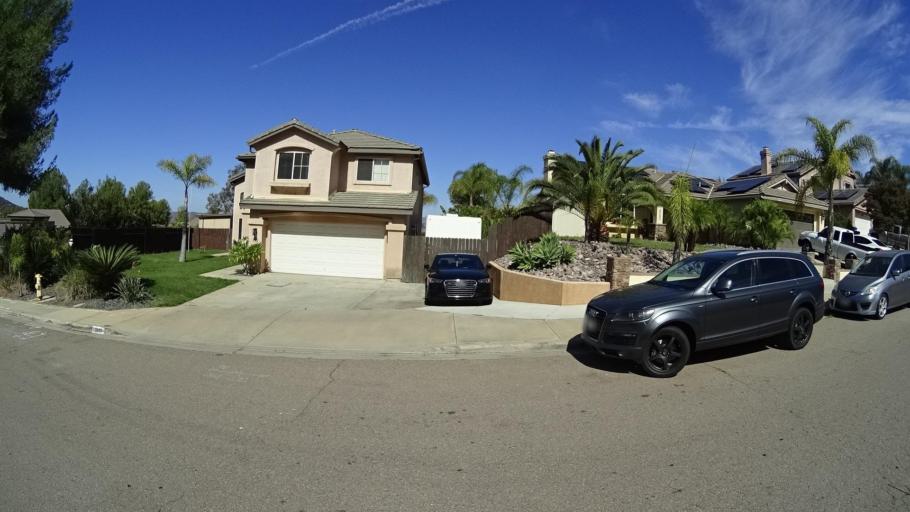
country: US
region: California
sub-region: San Diego County
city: Granite Hills
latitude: 32.8275
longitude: -116.8991
